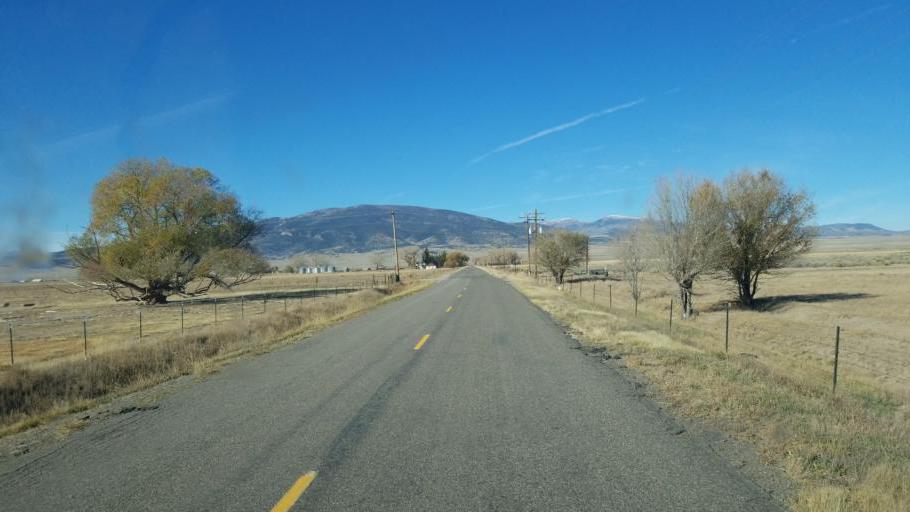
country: US
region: Colorado
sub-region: Rio Grande County
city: Monte Vista
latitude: 37.4590
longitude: -106.1290
